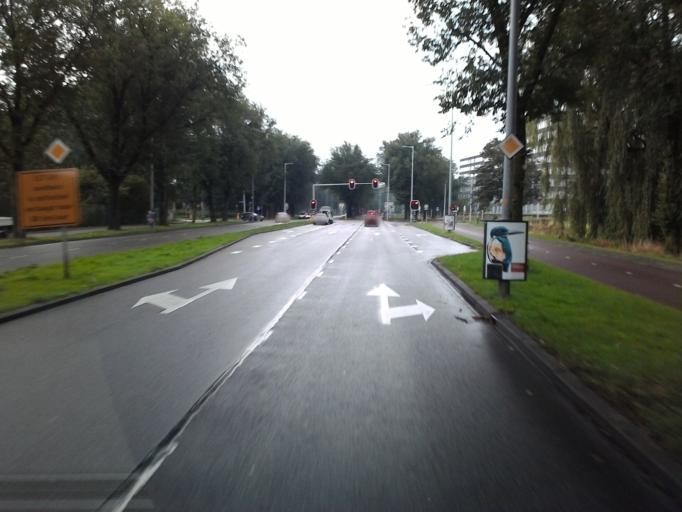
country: NL
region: Utrecht
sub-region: Gemeente Utrecht
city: Utrecht
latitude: 52.1079
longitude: 5.1137
